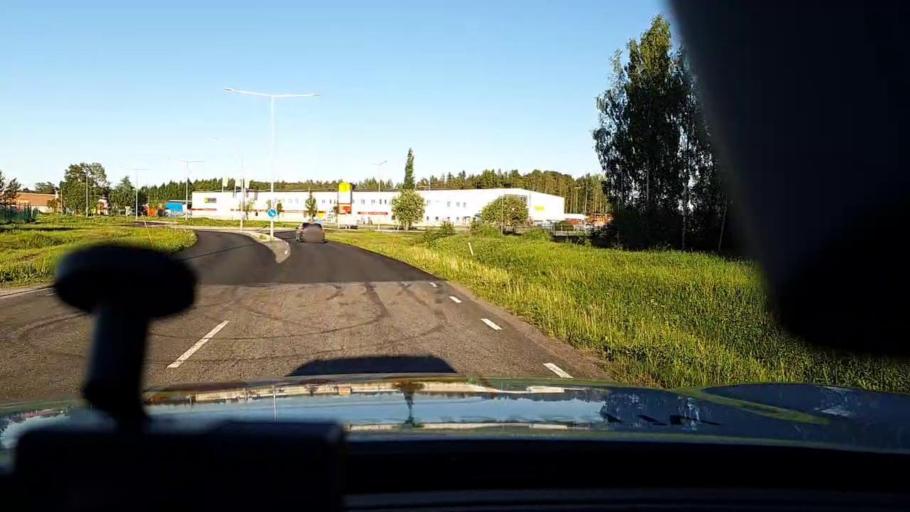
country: SE
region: Norrbotten
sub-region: Lulea Kommun
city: Bergnaset
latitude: 65.6119
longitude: 22.1198
